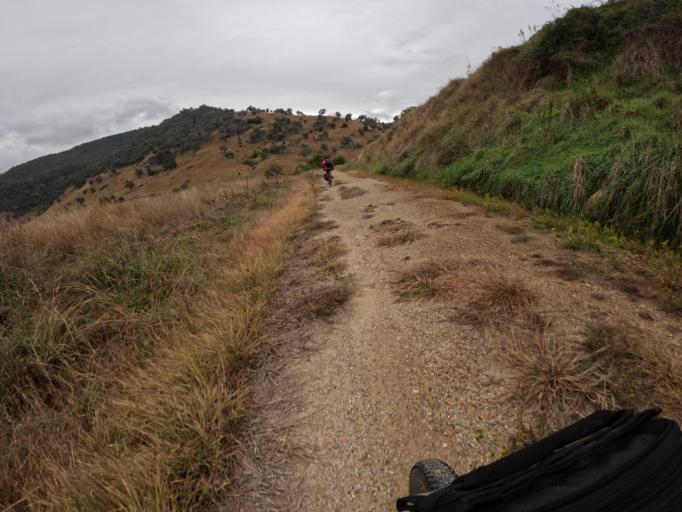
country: AU
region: New South Wales
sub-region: Albury Municipality
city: East Albury
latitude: -36.1848
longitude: 147.3588
